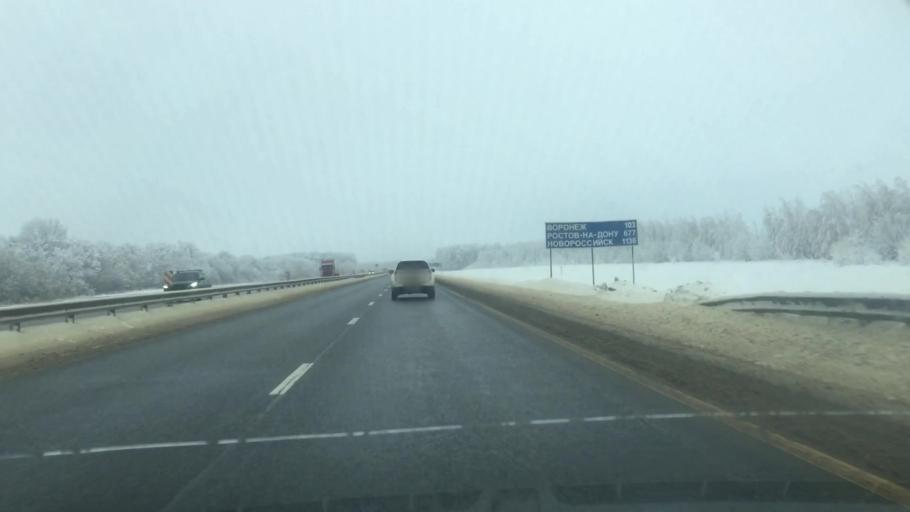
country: RU
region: Lipetsk
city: Zadonsk
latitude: 52.4988
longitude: 38.7553
